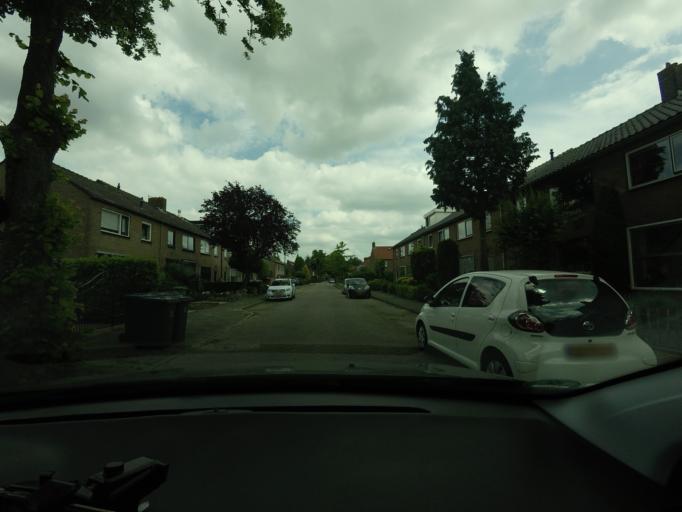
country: NL
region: Utrecht
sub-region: Stichtse Vecht
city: Maarssen
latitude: 52.0816
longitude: 5.0339
